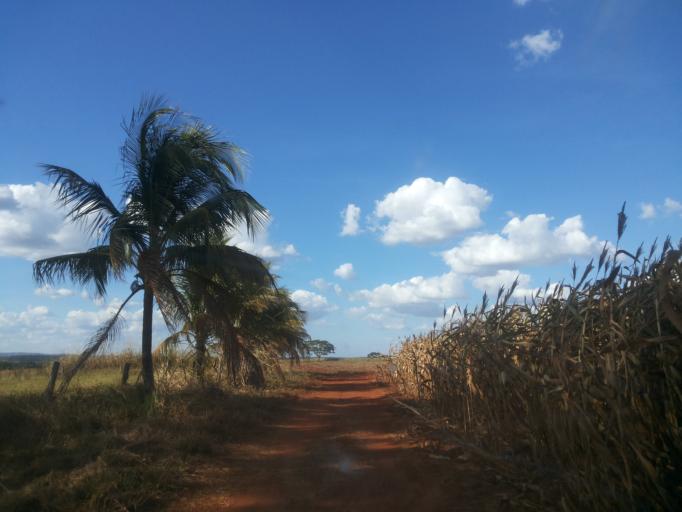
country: BR
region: Minas Gerais
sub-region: Capinopolis
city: Capinopolis
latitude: -18.5867
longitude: -49.4956
